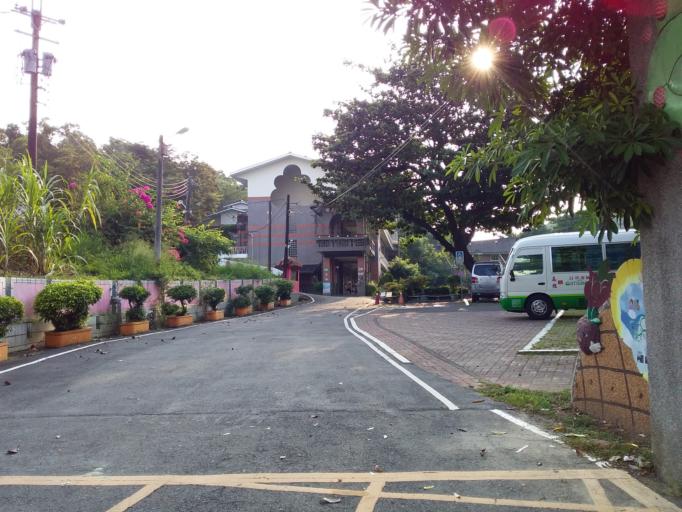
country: TW
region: Taiwan
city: Fengshan
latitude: 22.6889
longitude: 120.4092
